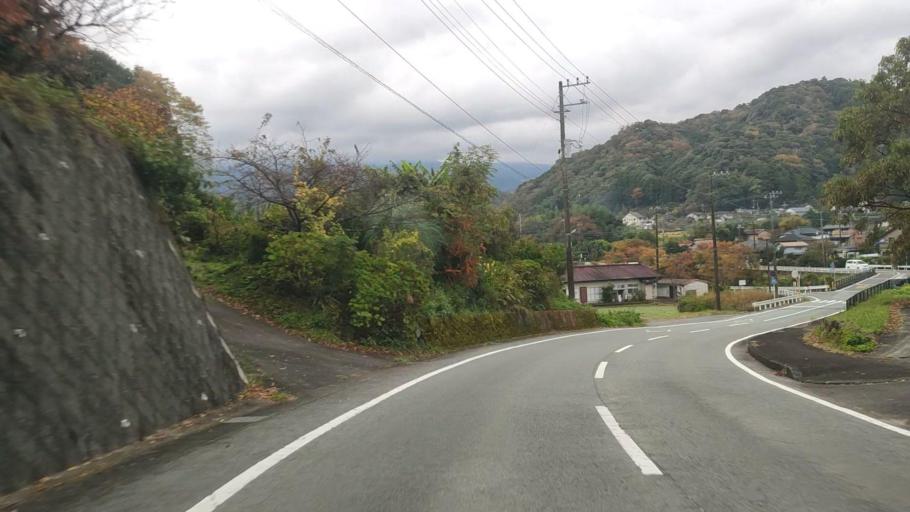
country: JP
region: Shizuoka
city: Ito
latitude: 34.9470
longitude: 138.9977
